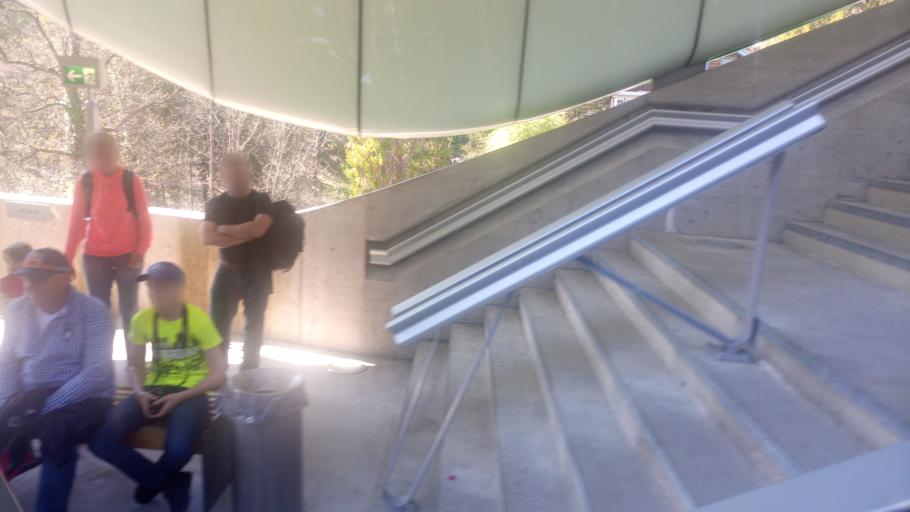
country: AT
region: Tyrol
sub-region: Innsbruck Stadt
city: Innsbruck
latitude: 47.2791
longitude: 11.3992
